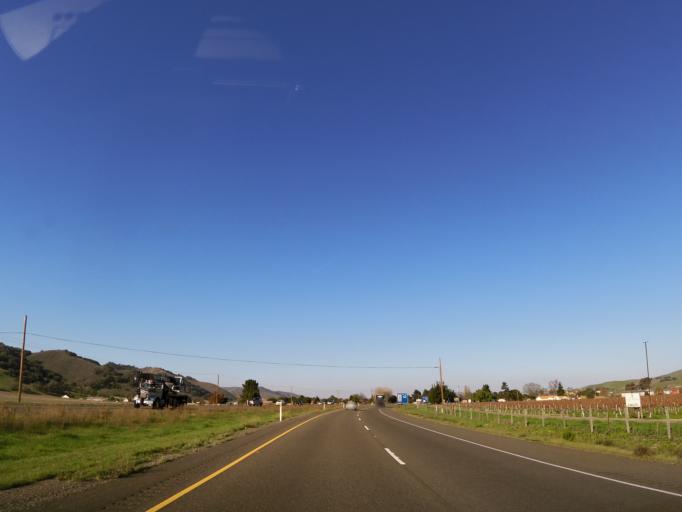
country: US
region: California
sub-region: Santa Barbara County
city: Los Alamos
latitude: 34.7376
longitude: -120.2619
